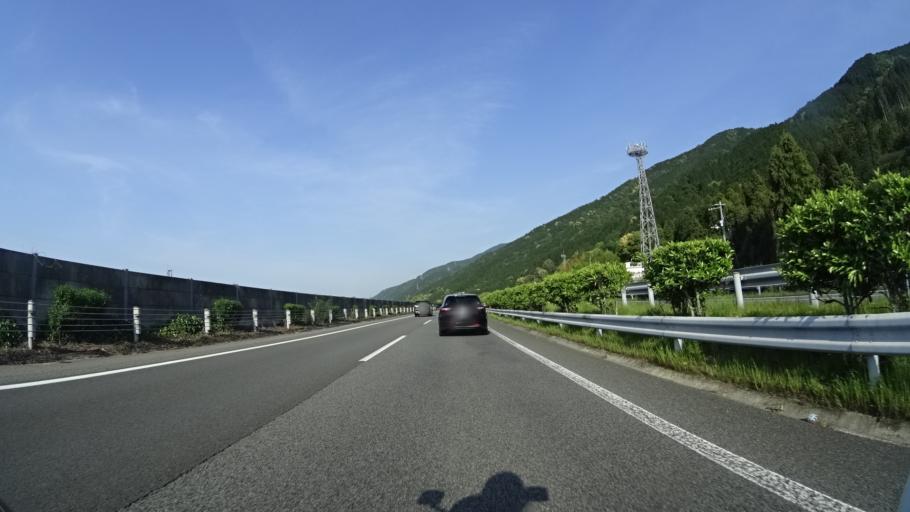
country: JP
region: Ehime
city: Niihama
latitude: 33.9175
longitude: 133.2912
